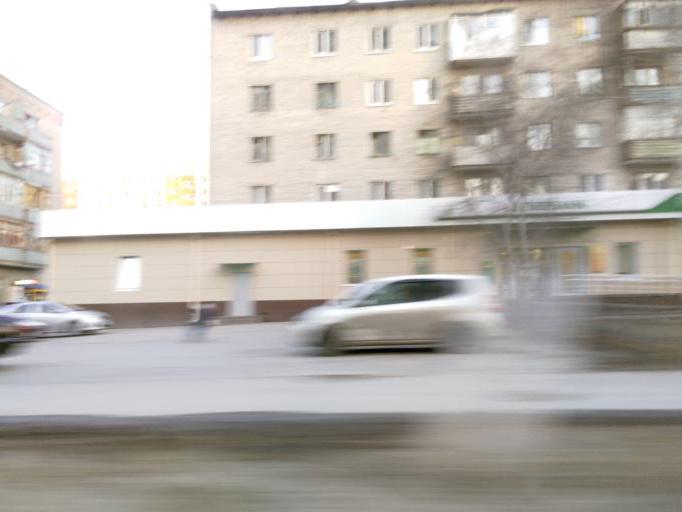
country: RU
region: Tjumen
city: Tyumen
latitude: 57.1608
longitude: 65.4932
